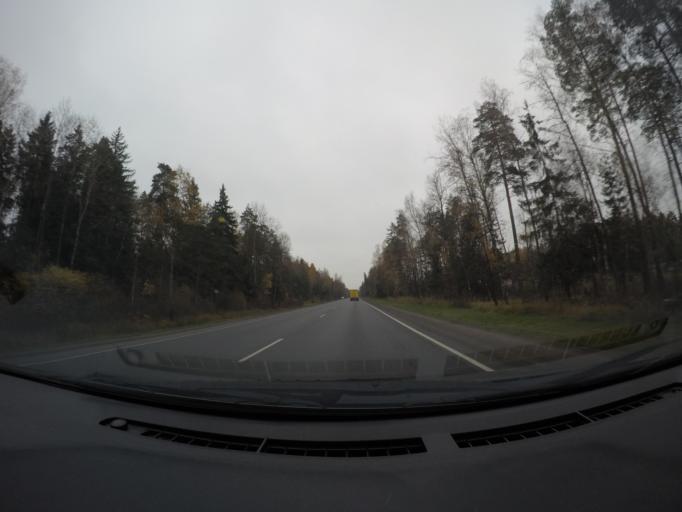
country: RU
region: Moskovskaya
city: Gzhel'
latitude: 55.5485
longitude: 38.4019
